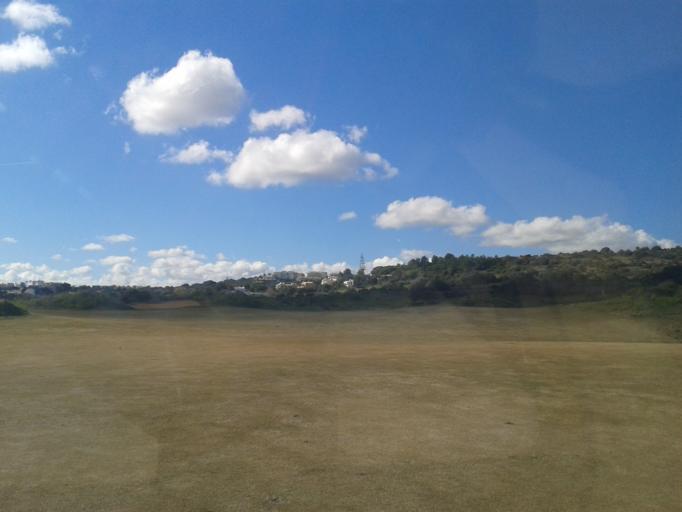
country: PT
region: Faro
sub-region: Lagos
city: Lagos
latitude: 37.1223
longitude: -8.6396
